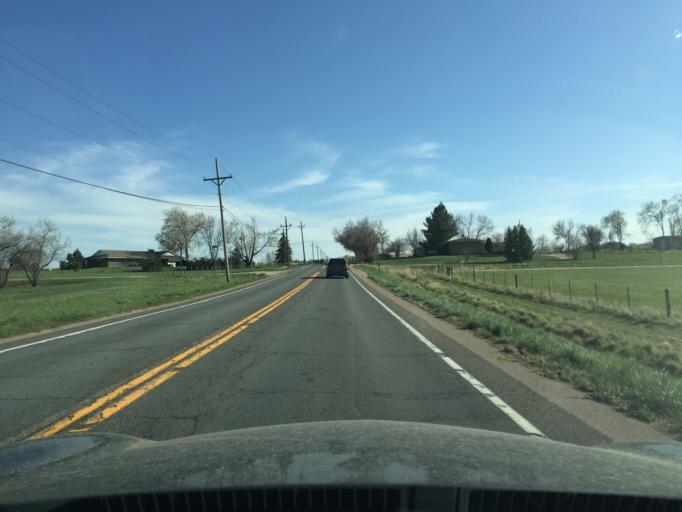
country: US
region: Colorado
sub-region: Boulder County
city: Niwot
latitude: 40.1107
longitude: -105.1313
